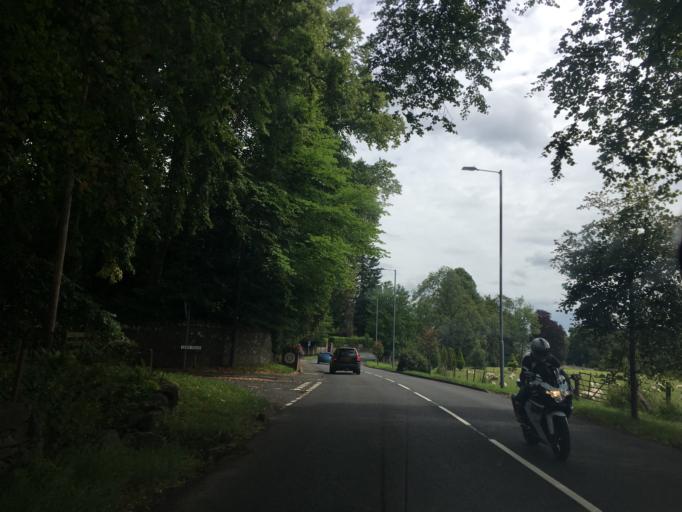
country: GB
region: Scotland
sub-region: Stirling
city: Callander
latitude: 56.2455
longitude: -4.2314
